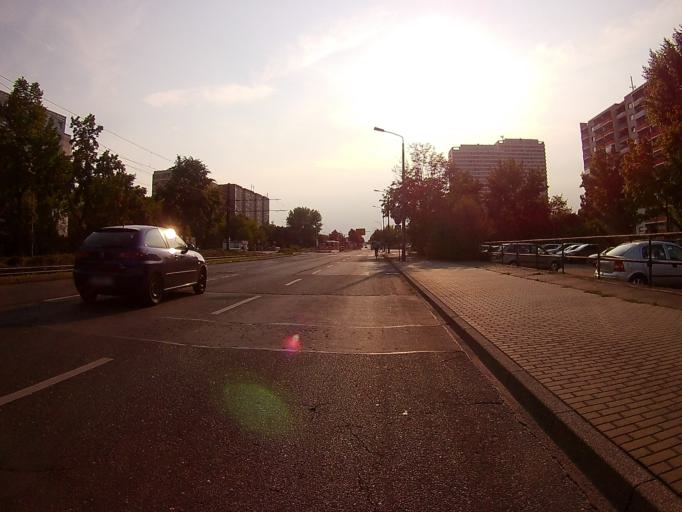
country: DE
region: Berlin
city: Biesdorf
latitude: 52.5261
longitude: 13.5454
